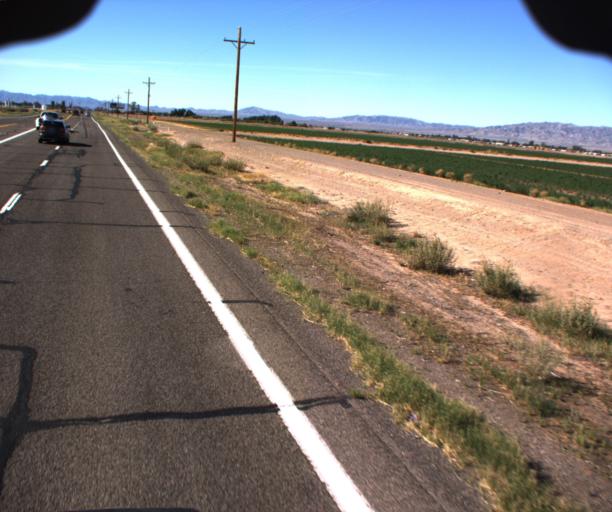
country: US
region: Arizona
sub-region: Mohave County
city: Mohave Valley
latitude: 34.9325
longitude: -114.5980
